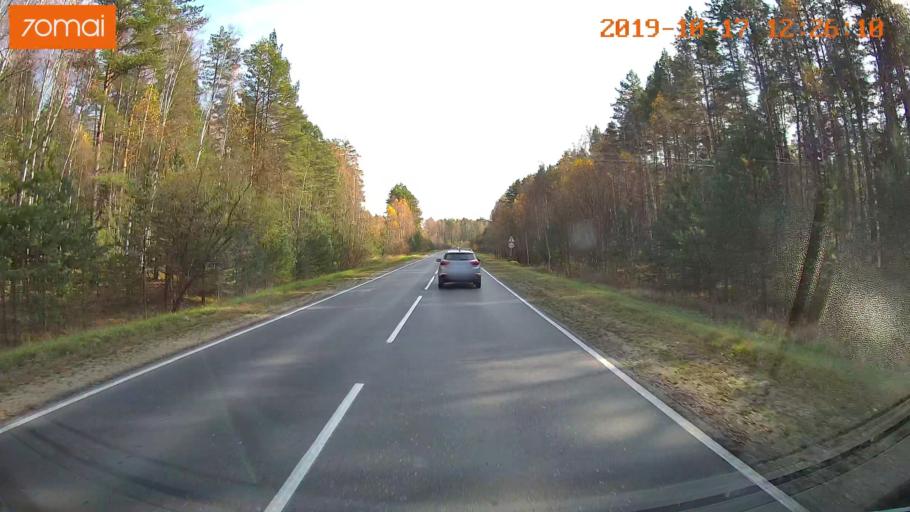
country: RU
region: Rjazan
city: Syntul
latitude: 55.0215
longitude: 41.2511
